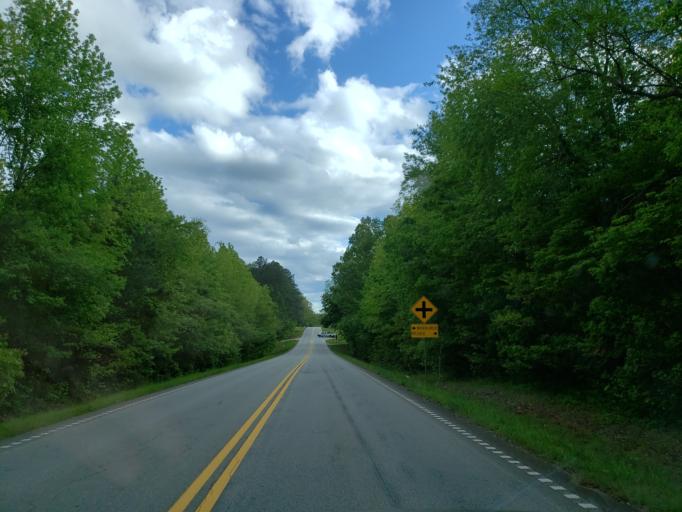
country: US
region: Georgia
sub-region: Haralson County
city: Tallapoosa
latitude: 33.8463
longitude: -85.2923
